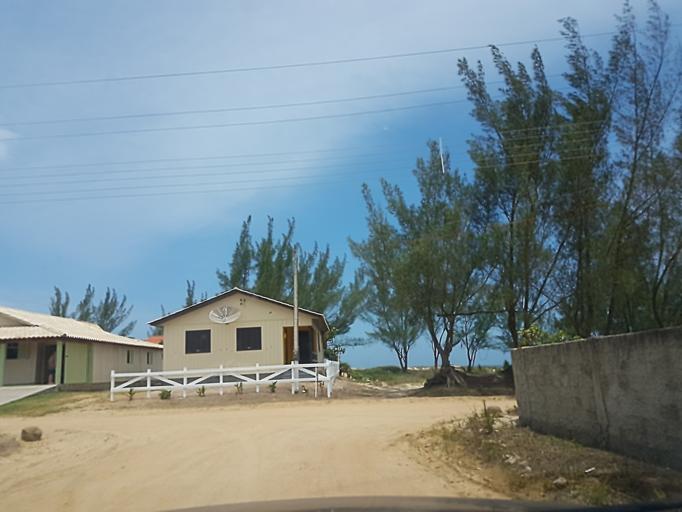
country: BR
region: Santa Catarina
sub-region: Jaguaruna
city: Jaguaruna
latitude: -28.6633
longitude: -48.9622
